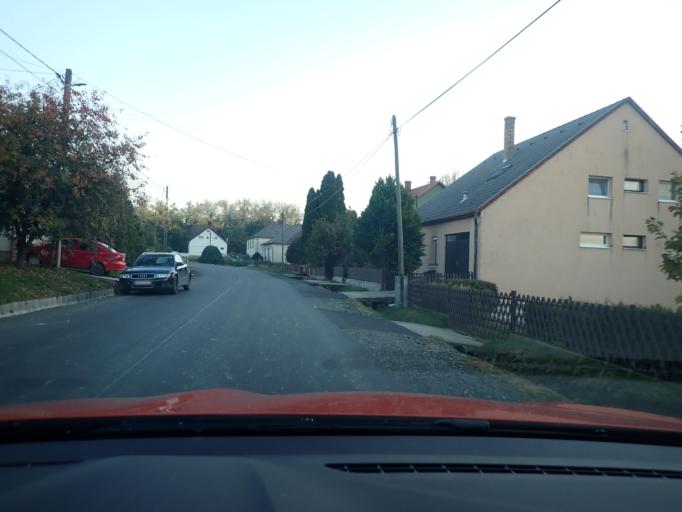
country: HU
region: Baranya
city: Kozarmisleny
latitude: 46.0304
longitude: 18.3901
